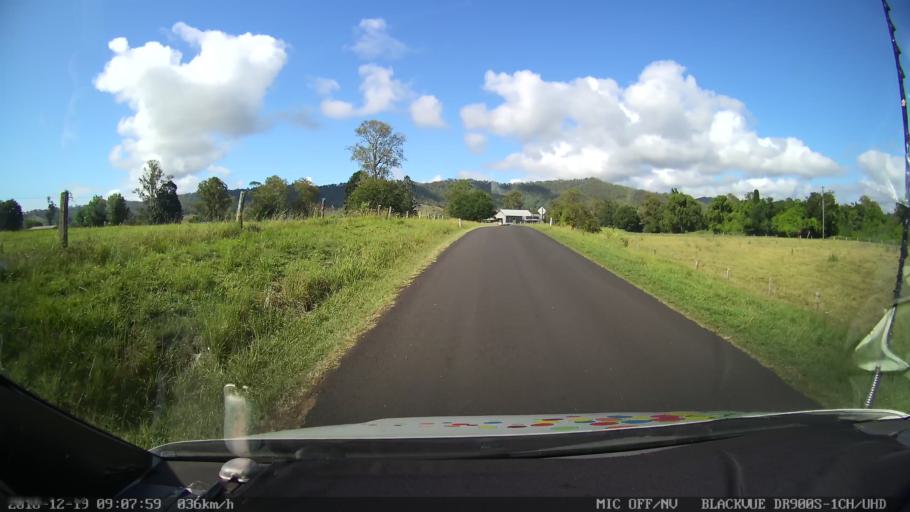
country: AU
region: New South Wales
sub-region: Kyogle
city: Kyogle
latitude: -28.4780
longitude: 152.9325
